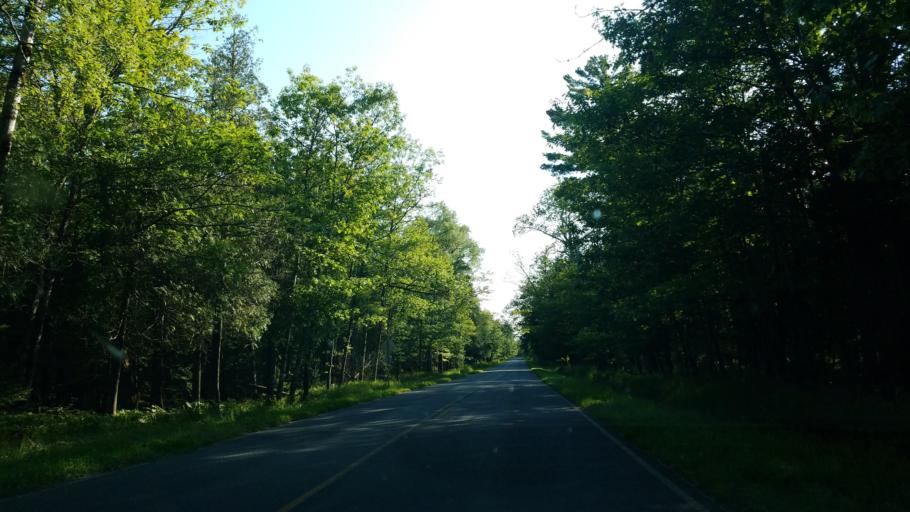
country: US
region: Wisconsin
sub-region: Bayfield County
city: Washburn
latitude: 46.7672
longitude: -90.7500
